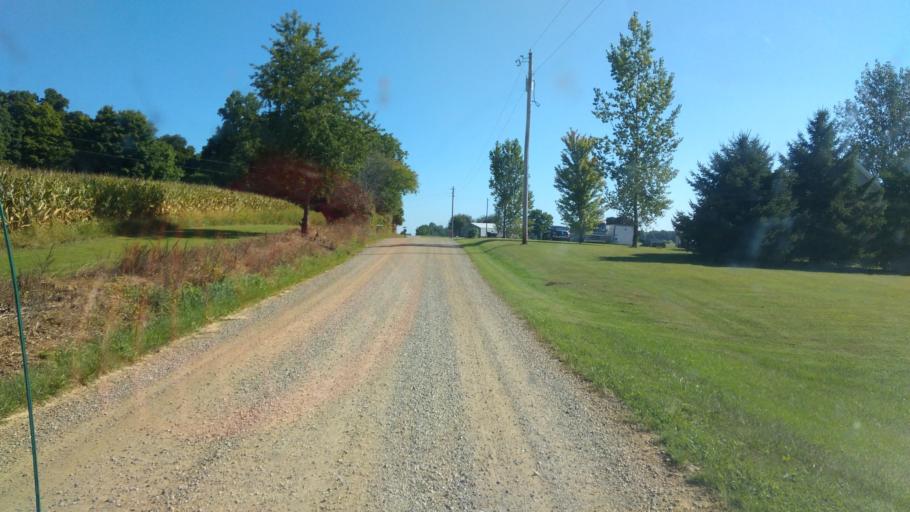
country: US
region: Ohio
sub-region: Knox County
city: Gambier
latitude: 40.4926
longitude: -82.4046
